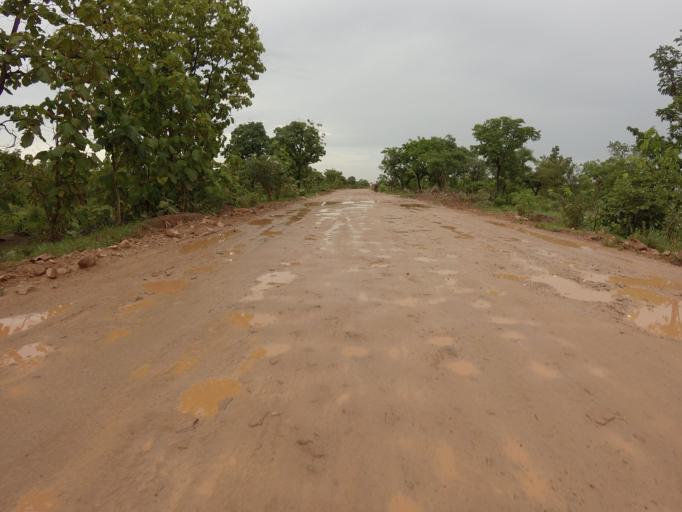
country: GH
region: Upper East
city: Bolgatanga
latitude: 10.8783
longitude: -0.6336
